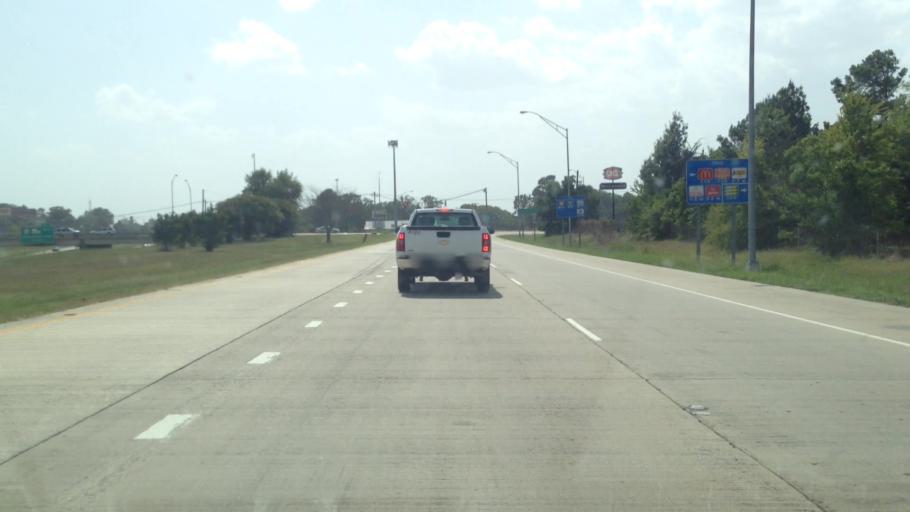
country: US
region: Louisiana
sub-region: Caddo Parish
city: Greenwood
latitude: 32.4513
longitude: -93.8634
